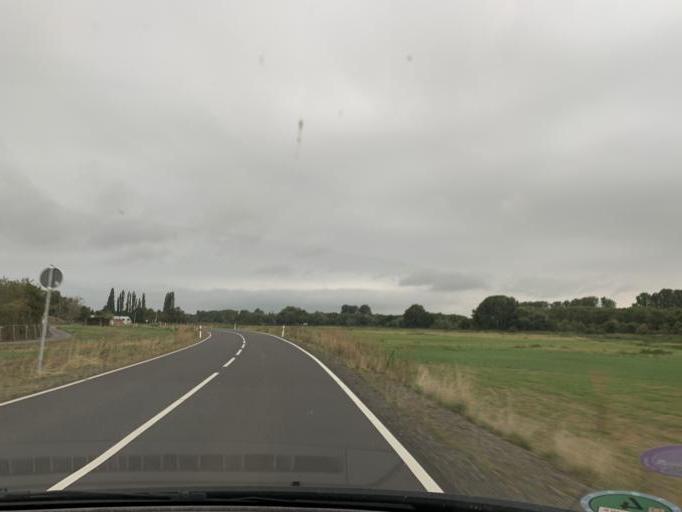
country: DE
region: North Rhine-Westphalia
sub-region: Regierungsbezirk Koln
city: Niederzier
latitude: 50.8442
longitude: 6.4359
